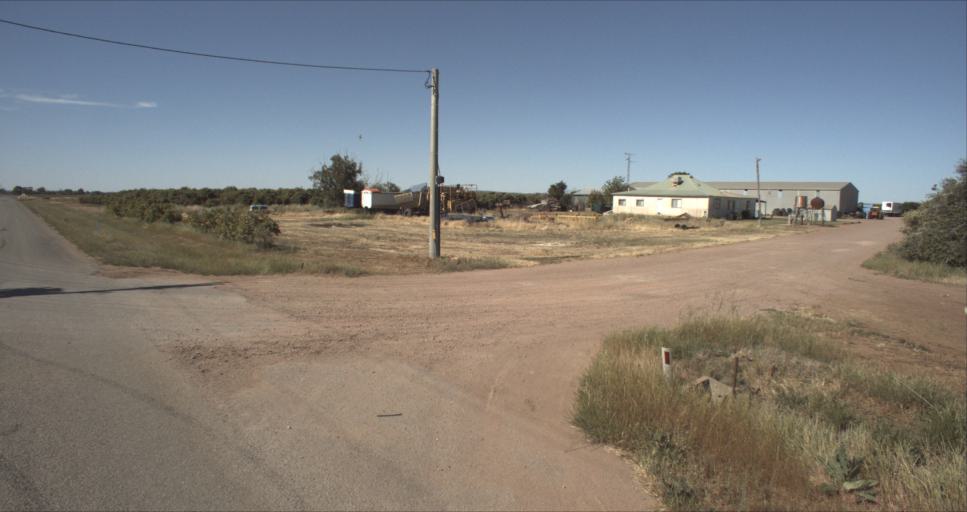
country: AU
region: New South Wales
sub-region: Leeton
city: Leeton
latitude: -34.5863
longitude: 146.3789
